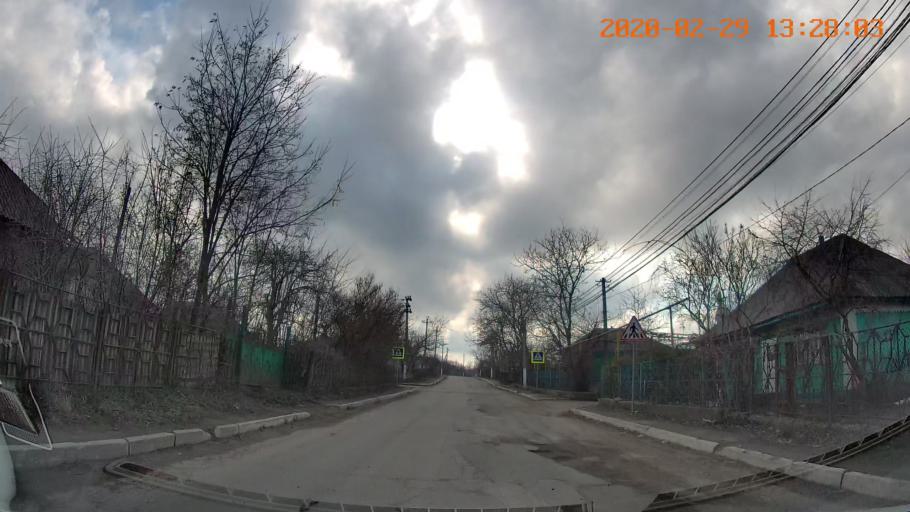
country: MD
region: Telenesti
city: Camenca
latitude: 47.9083
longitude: 28.6441
